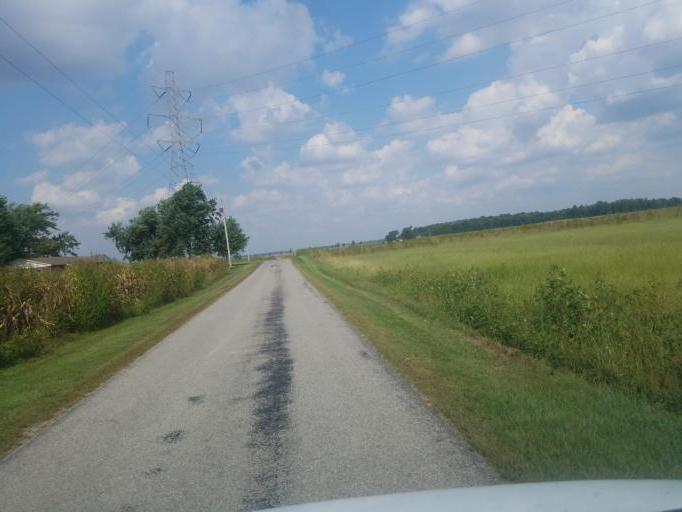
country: US
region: Ohio
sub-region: Hardin County
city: Ada
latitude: 40.6272
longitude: -83.7881
